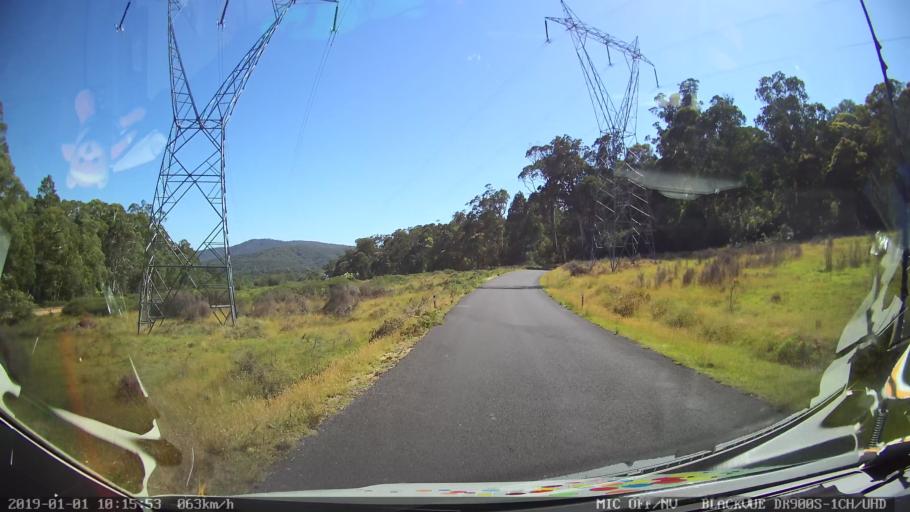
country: AU
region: New South Wales
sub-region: Snowy River
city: Jindabyne
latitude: -36.0974
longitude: 148.1627
